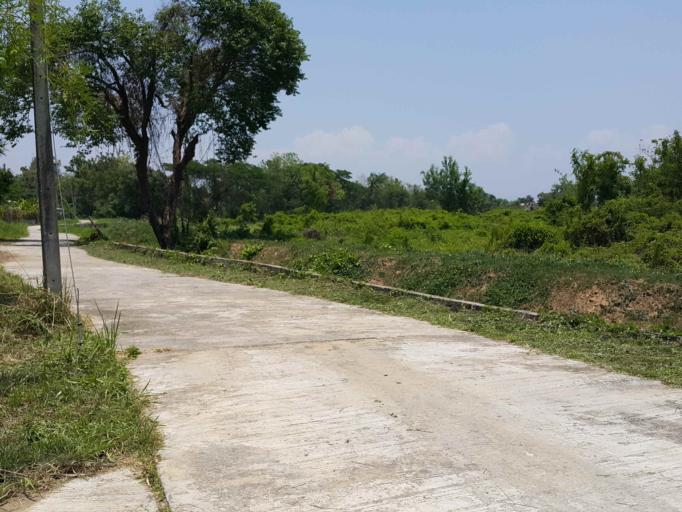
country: TH
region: Chiang Mai
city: San Kamphaeng
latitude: 18.8081
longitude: 99.1151
